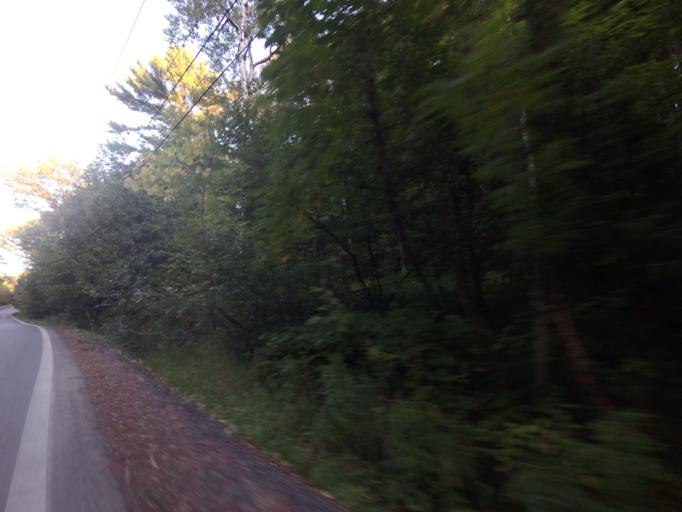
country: CA
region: Quebec
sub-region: Monteregie
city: Hudson
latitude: 45.4684
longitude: -74.1676
